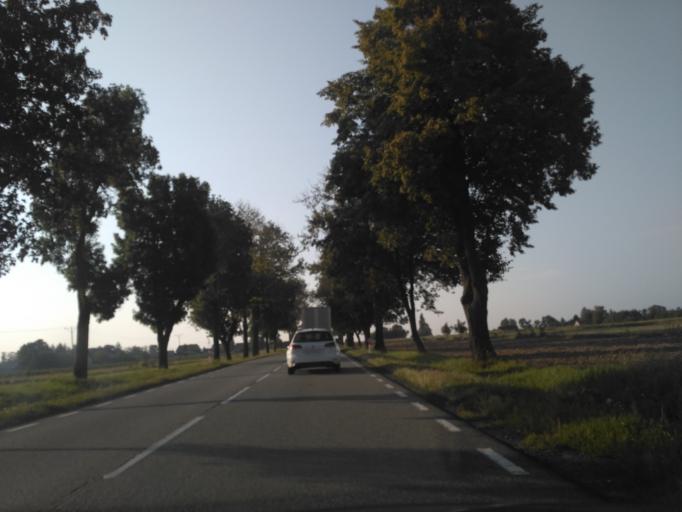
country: PL
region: Lublin Voivodeship
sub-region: Powiat krasnicki
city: Szastarka
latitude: 50.8352
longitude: 22.3039
